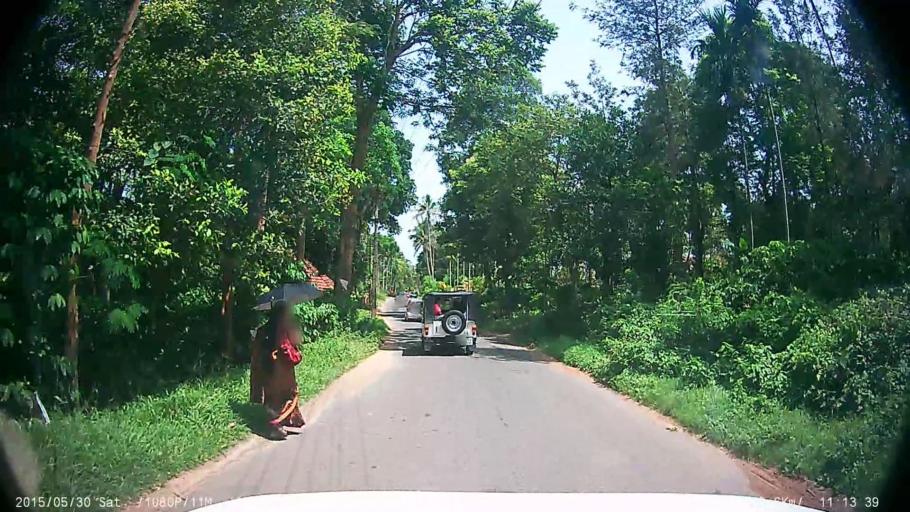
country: IN
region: Kerala
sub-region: Wayanad
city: Panamaram
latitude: 11.7628
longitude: 76.0633
